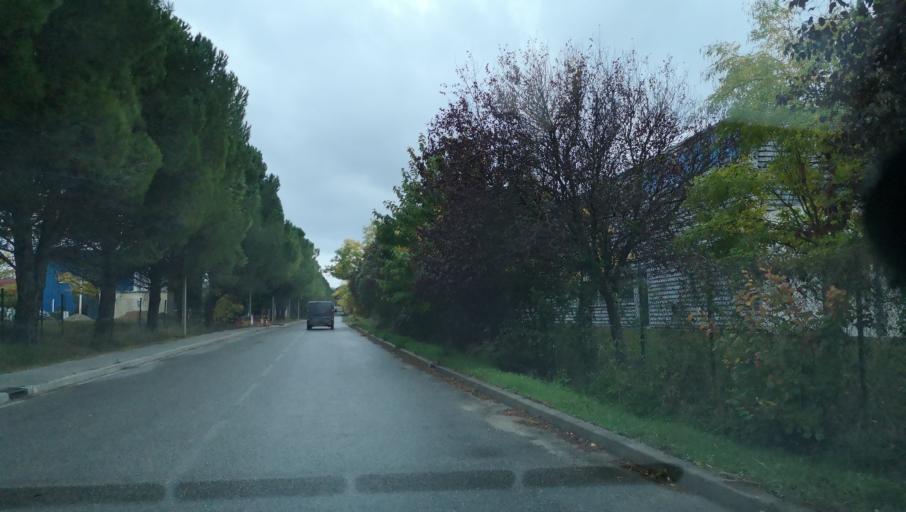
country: FR
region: Provence-Alpes-Cote d'Azur
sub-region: Departement des Bouches-du-Rhone
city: Rousset
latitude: 43.4724
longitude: 5.6091
